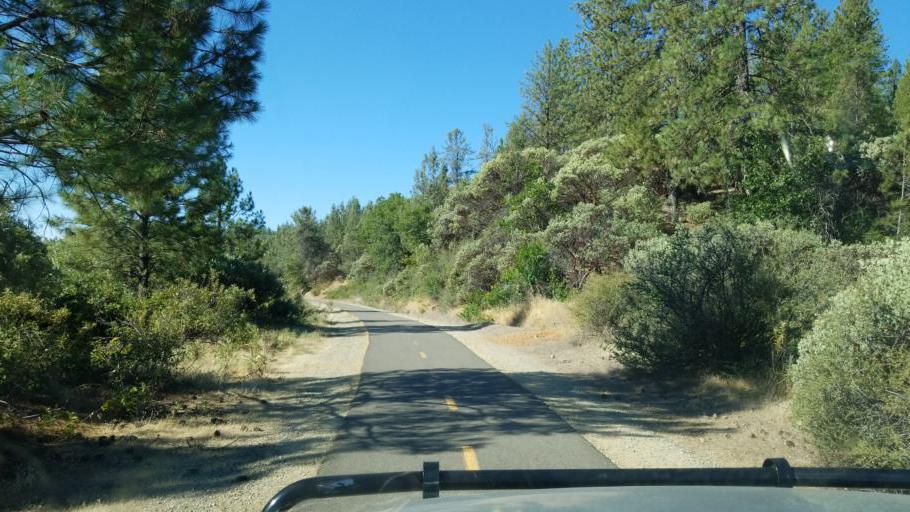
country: US
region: California
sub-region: Shasta County
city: Shasta
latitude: 40.6733
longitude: -122.4613
